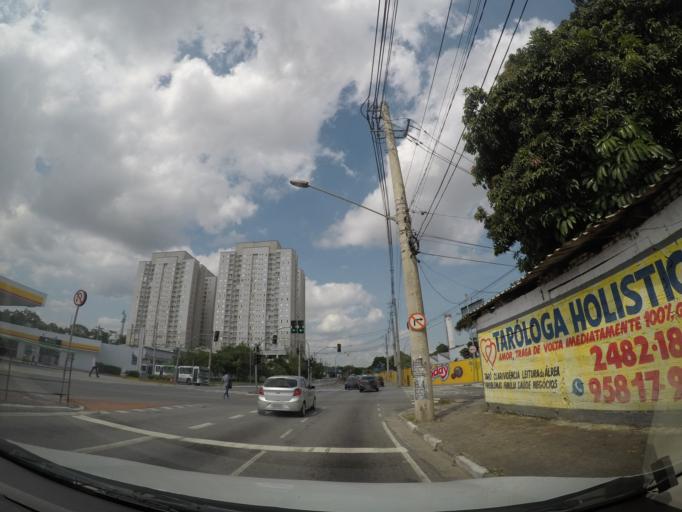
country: BR
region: Sao Paulo
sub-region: Guarulhos
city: Guarulhos
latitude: -23.4638
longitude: -46.4992
